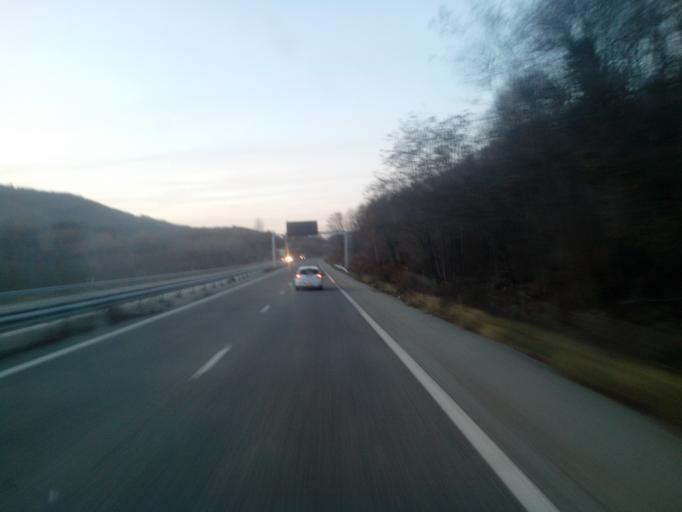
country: FR
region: Midi-Pyrenees
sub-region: Departement de l'Ariege
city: Montgaillard
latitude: 42.9298
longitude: 1.6310
